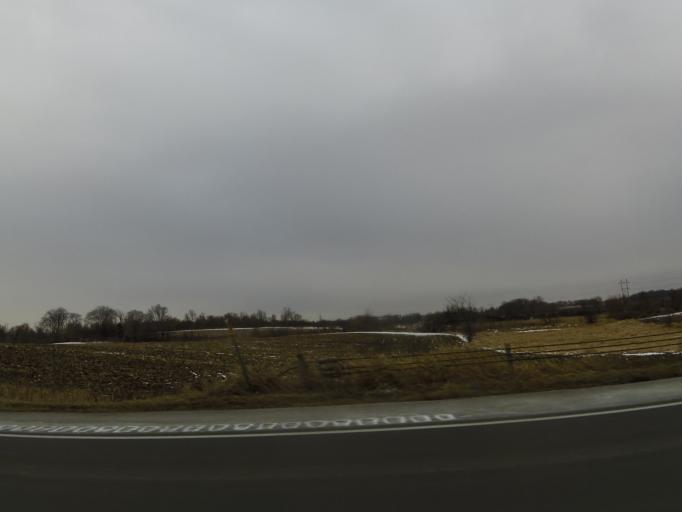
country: US
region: Minnesota
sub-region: Carver County
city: Young America (historical)
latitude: 44.7680
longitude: -93.8772
